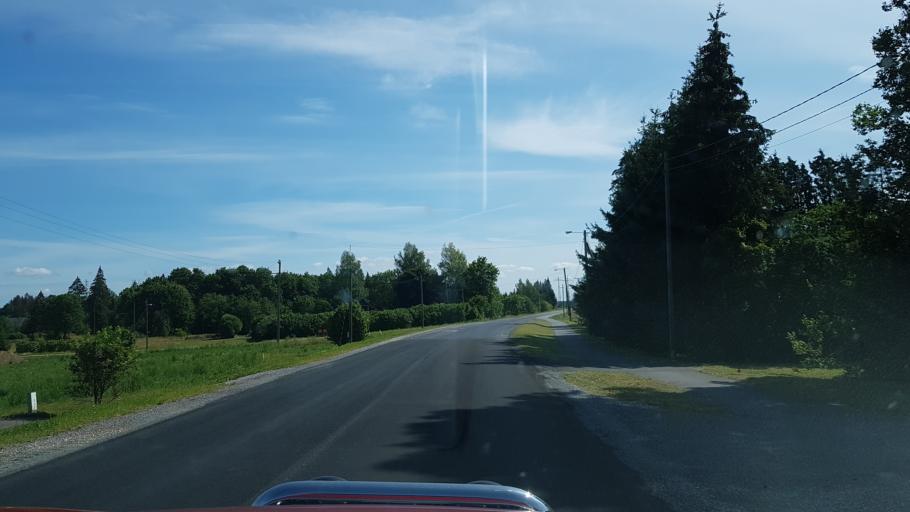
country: EE
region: Laeaene-Virumaa
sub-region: Tapa vald
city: Tapa
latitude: 59.1908
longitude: 25.8485
